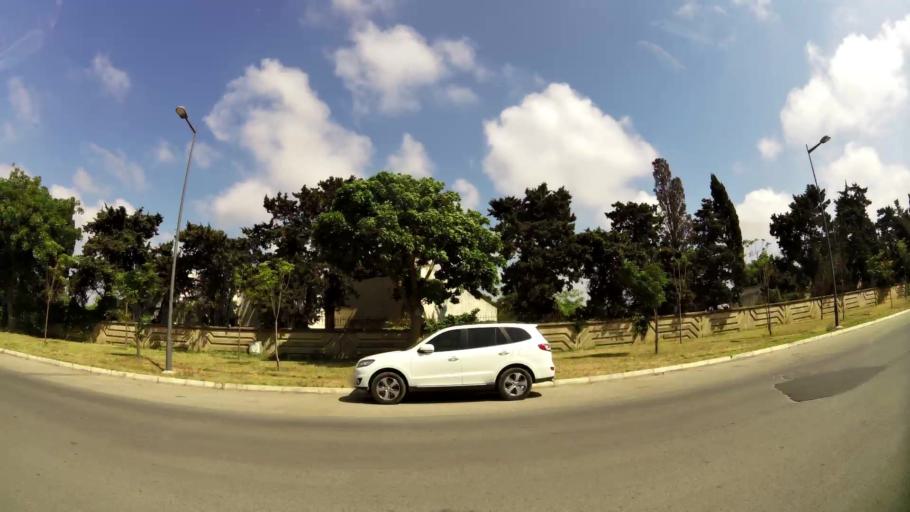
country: MA
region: Rabat-Sale-Zemmour-Zaer
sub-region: Rabat
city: Rabat
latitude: 33.9799
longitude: -6.8657
